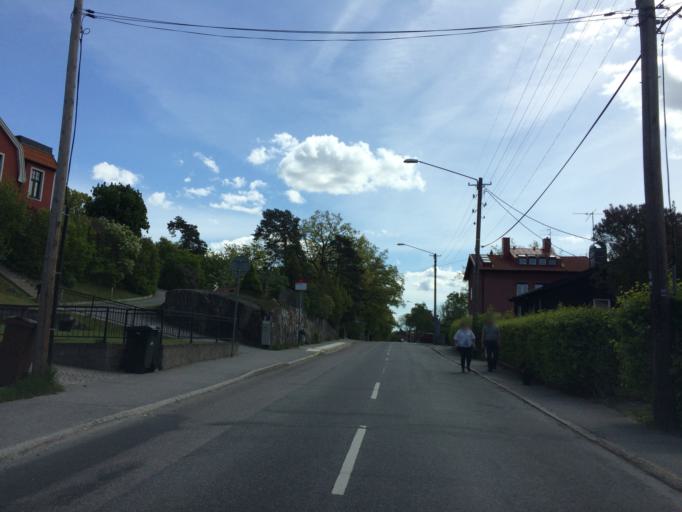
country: SE
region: Stockholm
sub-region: Huddinge Kommun
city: Huddinge
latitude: 59.2792
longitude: 17.9977
